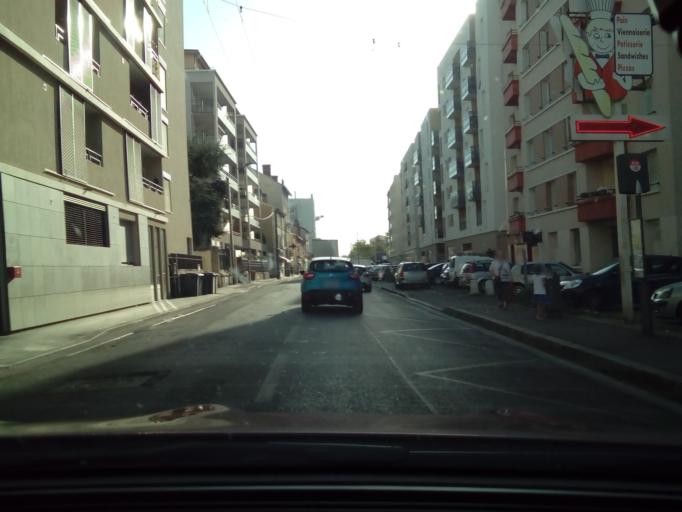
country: FR
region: Rhone-Alpes
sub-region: Departement du Rhone
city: Villeurbanne
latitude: 45.7601
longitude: 4.8983
